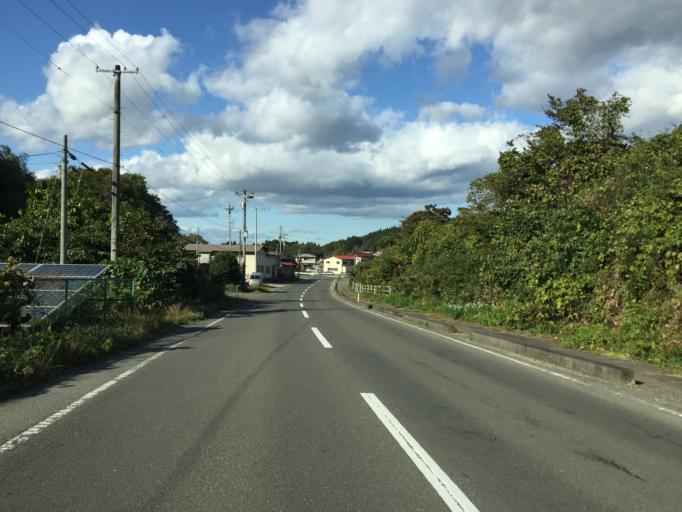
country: JP
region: Miyagi
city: Marumori
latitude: 37.8620
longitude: 140.8271
